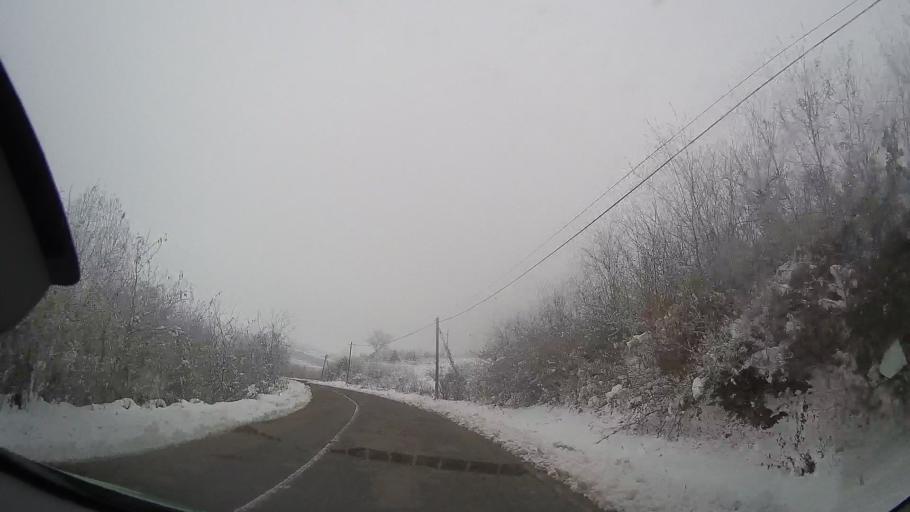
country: RO
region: Neamt
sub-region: Comuna Valea Ursului
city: Valea Ursului
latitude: 46.8040
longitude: 27.1017
